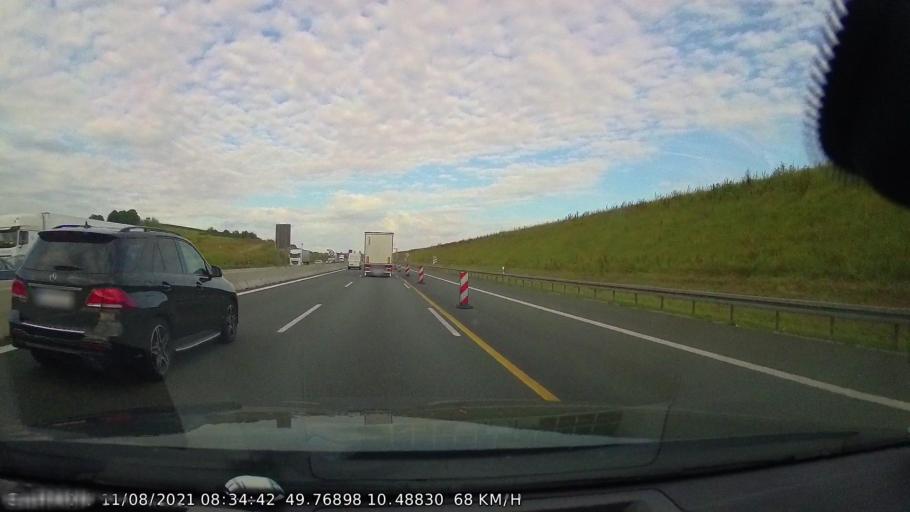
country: DE
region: Bavaria
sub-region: Regierungsbezirk Unterfranken
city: Geiselwind
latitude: 49.7692
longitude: 10.4890
